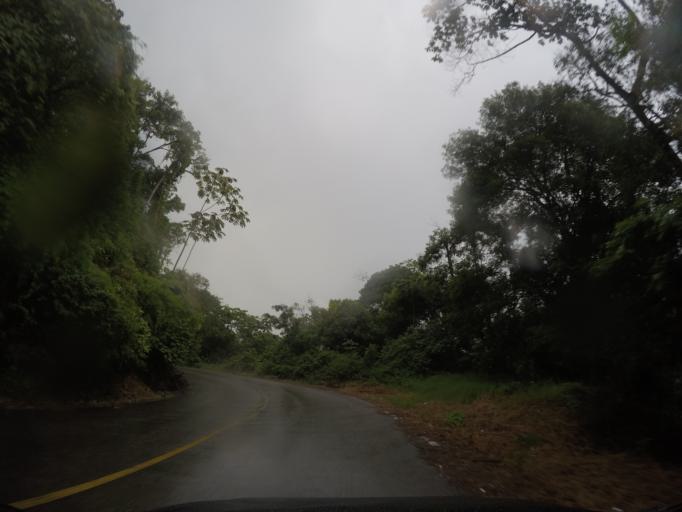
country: MX
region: Oaxaca
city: San Gabriel Mixtepec
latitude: 16.0814
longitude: -97.0800
